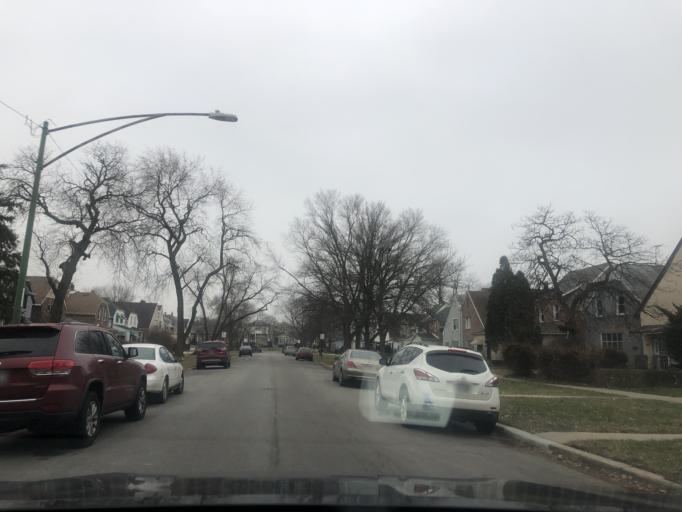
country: US
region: Illinois
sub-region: Cook County
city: Evergreen Park
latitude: 41.7344
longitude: -87.6225
